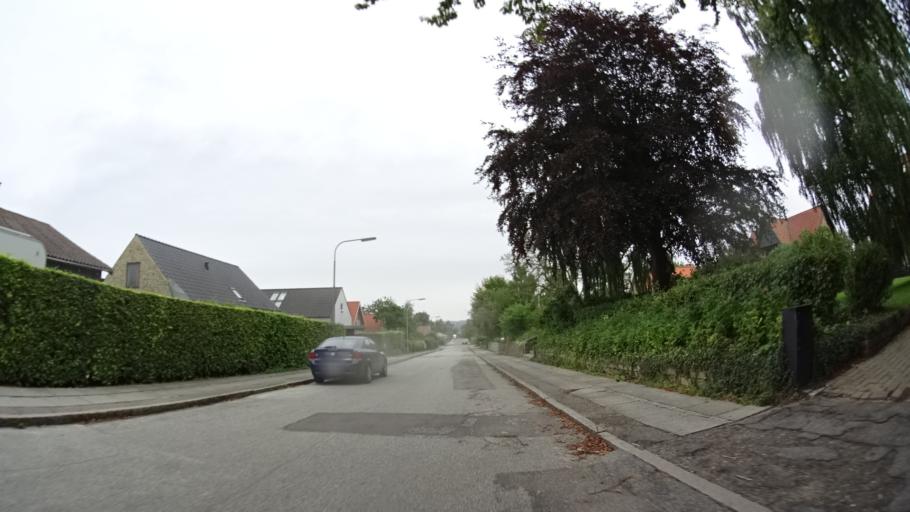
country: DK
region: Central Jutland
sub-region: Arhus Kommune
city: Arhus
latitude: 56.1631
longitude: 10.1619
